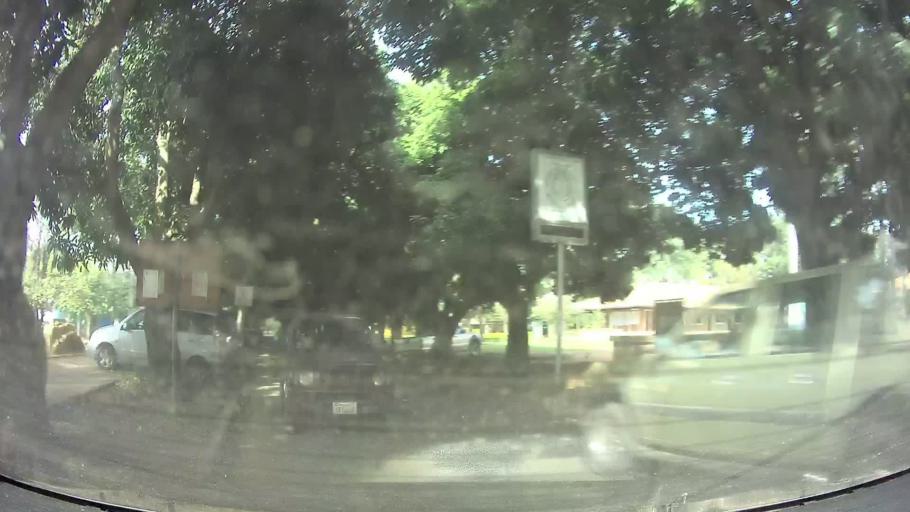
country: PY
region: Central
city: Fernando de la Mora
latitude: -25.3359
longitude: -57.5232
